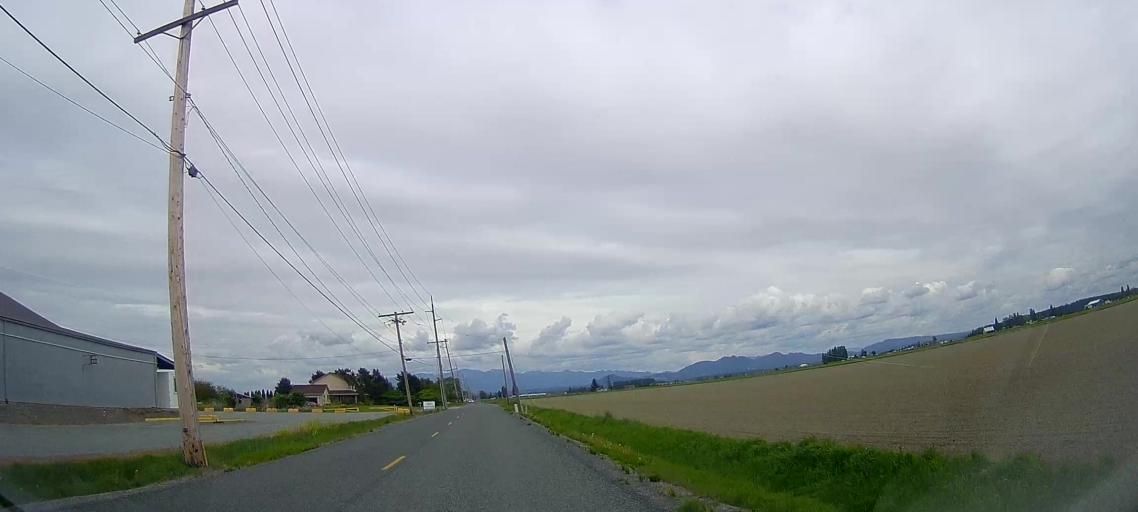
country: US
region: Washington
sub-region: Skagit County
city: Anacortes
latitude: 48.4208
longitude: -122.4886
